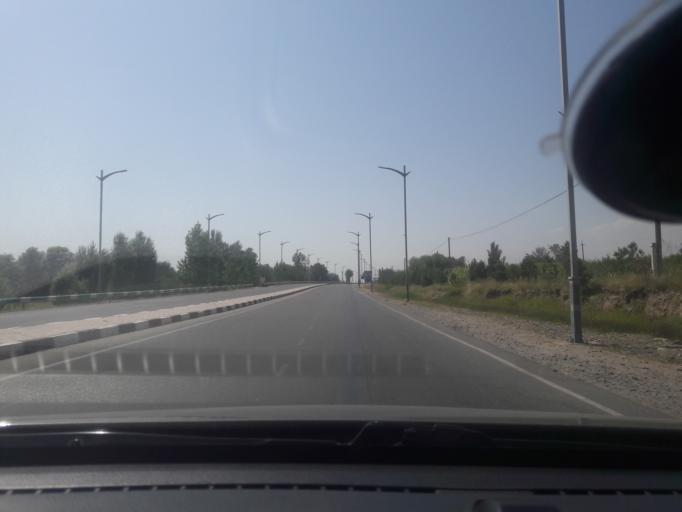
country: TJ
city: Shahrinav
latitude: 38.5640
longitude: 68.4070
